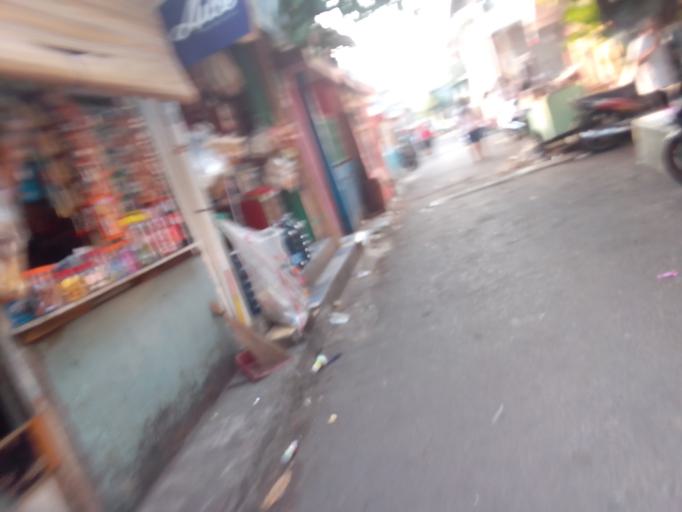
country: ID
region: Jakarta Raya
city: Jakarta
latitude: -6.1971
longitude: 106.8116
